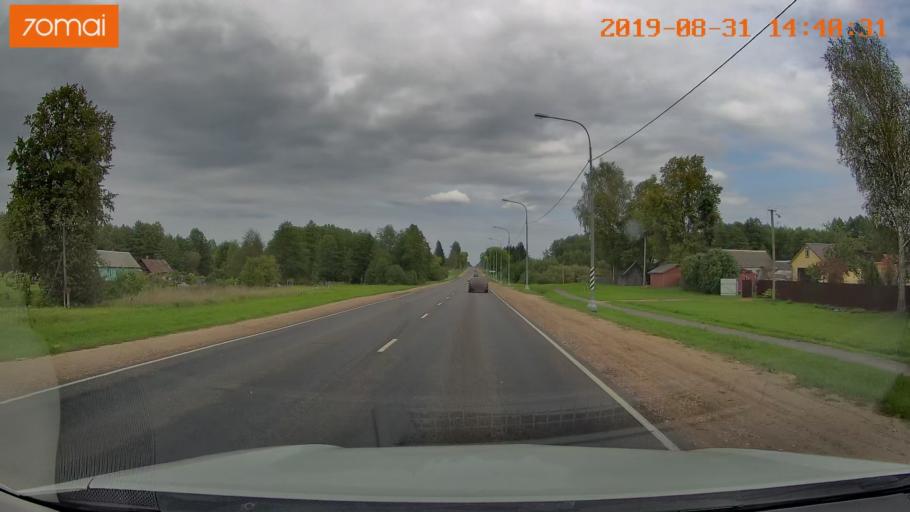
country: RU
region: Smolensk
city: Yekimovichi
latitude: 54.1976
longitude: 33.5729
